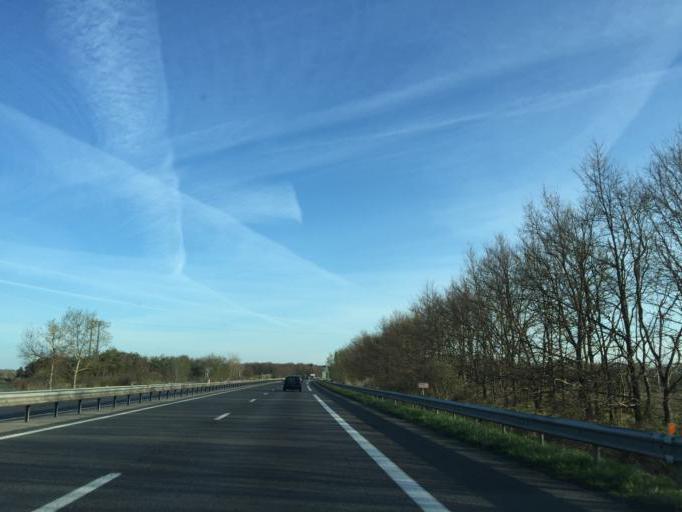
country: FR
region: Rhone-Alpes
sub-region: Departement de la Loire
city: Montrond-les-Bains
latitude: 45.6689
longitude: 4.1587
